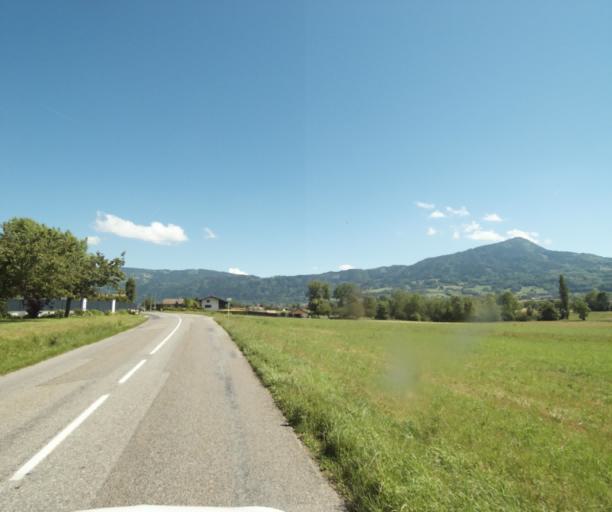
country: FR
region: Rhone-Alpes
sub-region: Departement de la Haute-Savoie
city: Ballaison
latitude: 46.2799
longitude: 6.3546
